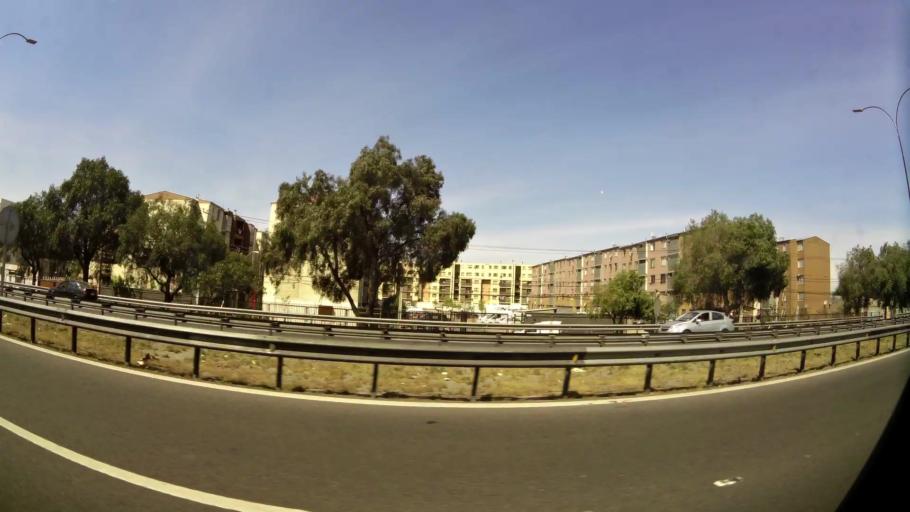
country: CL
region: Santiago Metropolitan
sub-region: Provincia de Maipo
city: San Bernardo
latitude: -33.5265
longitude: -70.6787
